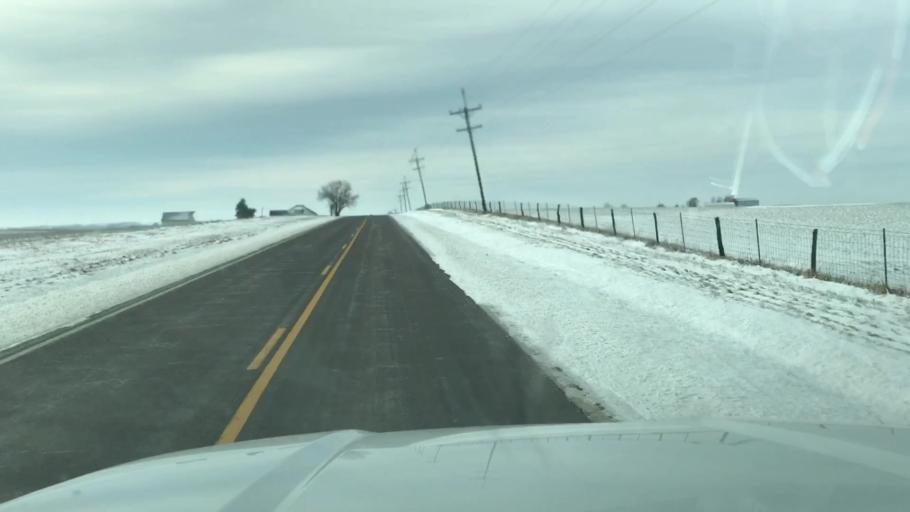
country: US
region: Missouri
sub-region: Holt County
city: Oregon
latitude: 40.0858
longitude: -95.1355
